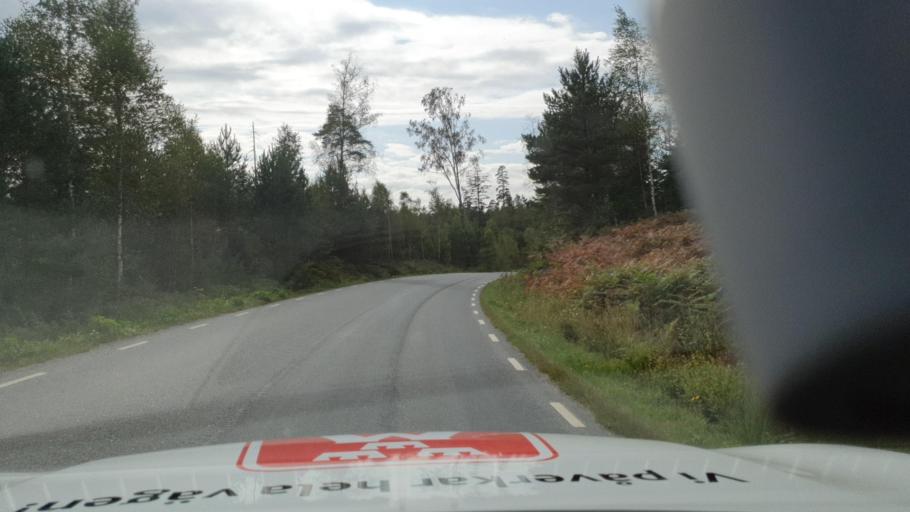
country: SE
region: Vaestra Goetaland
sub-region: Marks Kommun
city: Kinna
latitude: 57.3859
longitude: 12.7697
